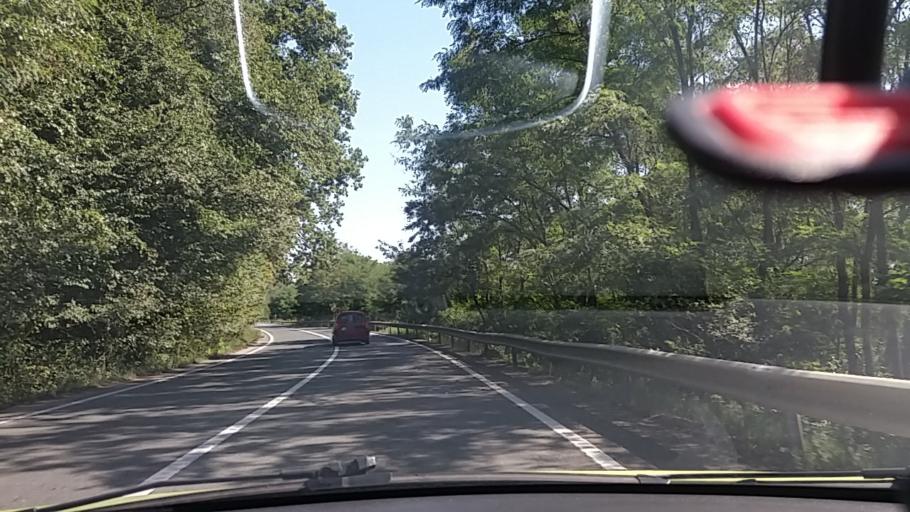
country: RO
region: Arad
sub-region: Comuna Barzava
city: Barzava
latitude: 46.1039
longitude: 21.9454
